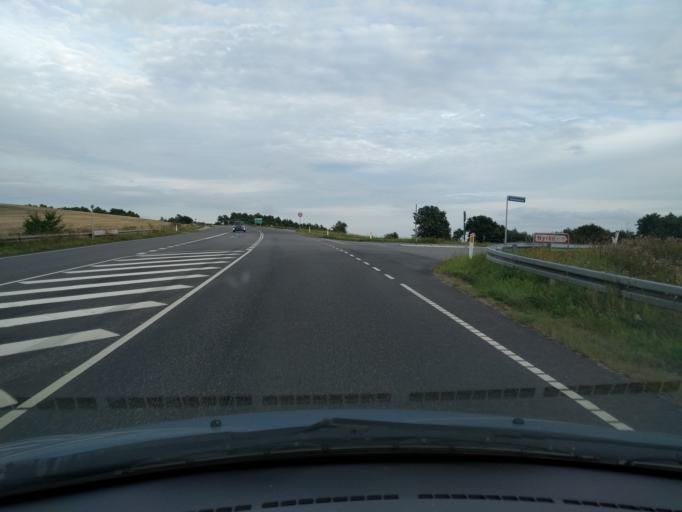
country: DK
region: Zealand
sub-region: Vordingborg Kommune
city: Nyrad
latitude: 55.0016
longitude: 11.9861
